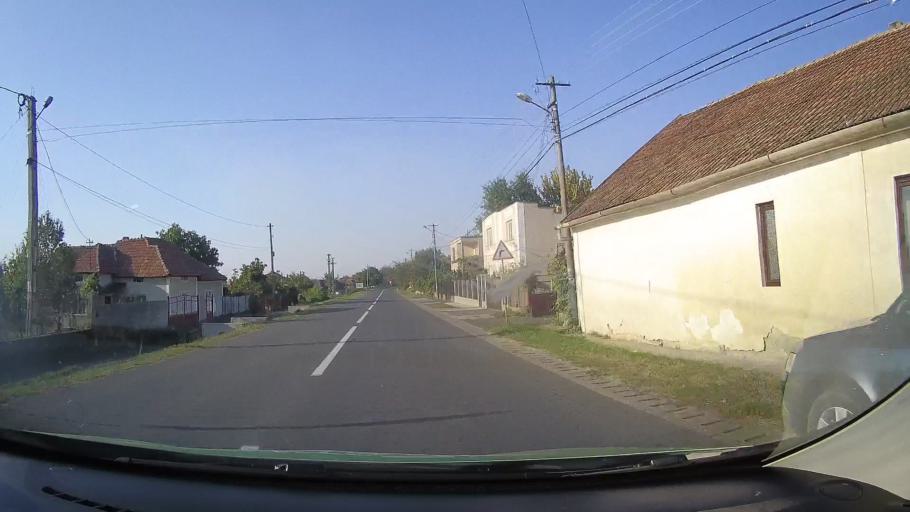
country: RO
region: Arad
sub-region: Comuna Ghioroc
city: Cuvin
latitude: 46.1602
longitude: 21.5924
